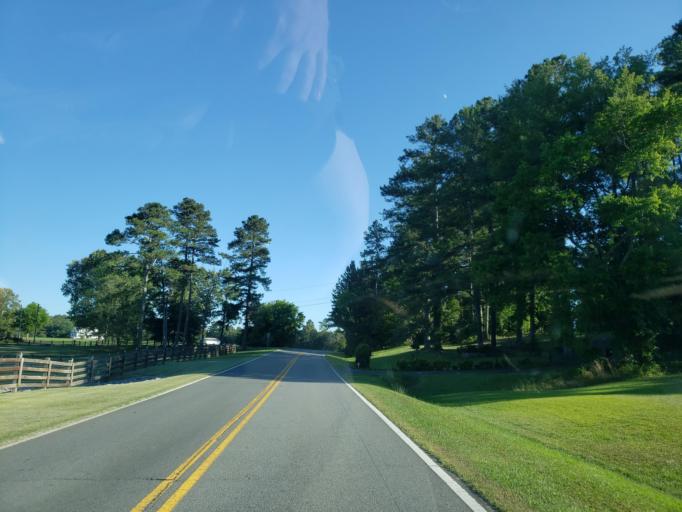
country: US
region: Georgia
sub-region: Floyd County
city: Shannon
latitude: 34.3687
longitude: -85.1327
